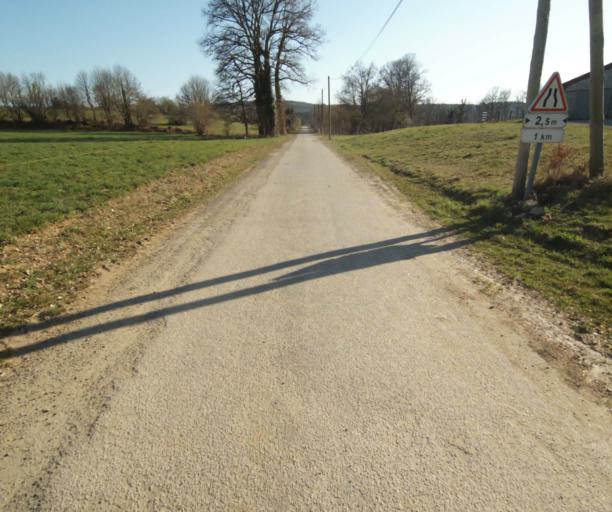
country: FR
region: Limousin
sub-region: Departement de la Correze
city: Chamboulive
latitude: 45.5015
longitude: 1.7257
